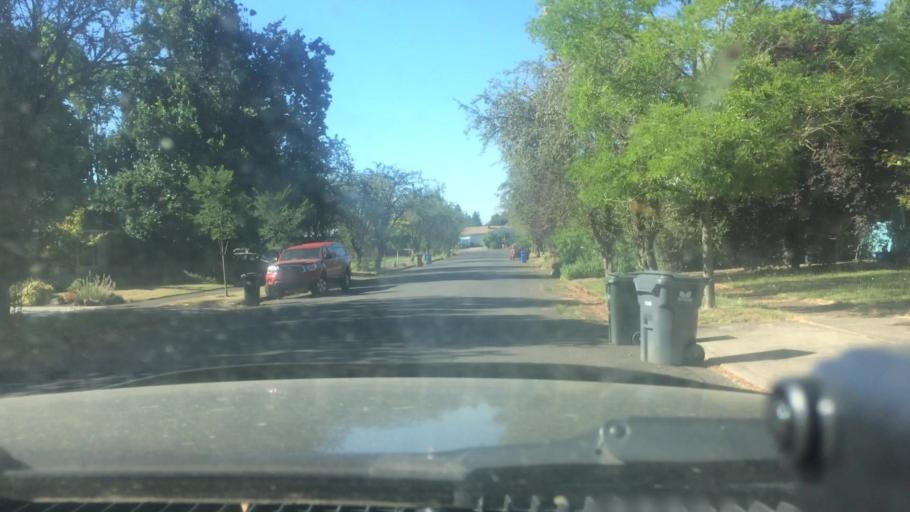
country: US
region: Oregon
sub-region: Lane County
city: Eugene
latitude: 44.0315
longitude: -123.1085
